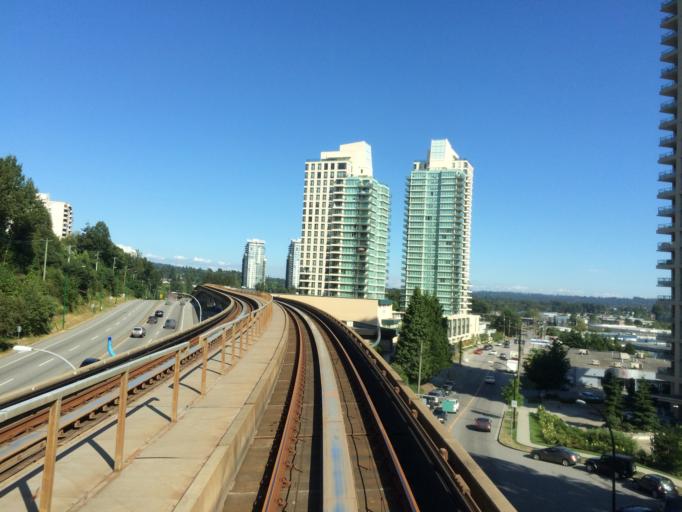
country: CA
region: British Columbia
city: Burnaby
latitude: 49.2650
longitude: -122.9925
